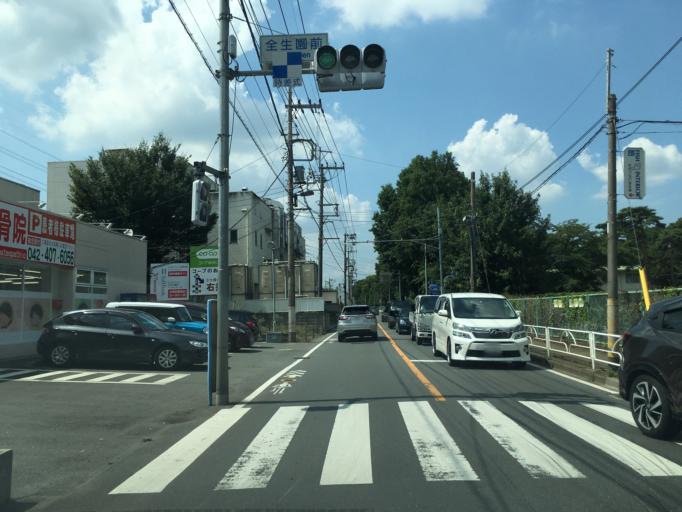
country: JP
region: Tokyo
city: Higashimurayama-shi
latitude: 35.7640
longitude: 139.4945
